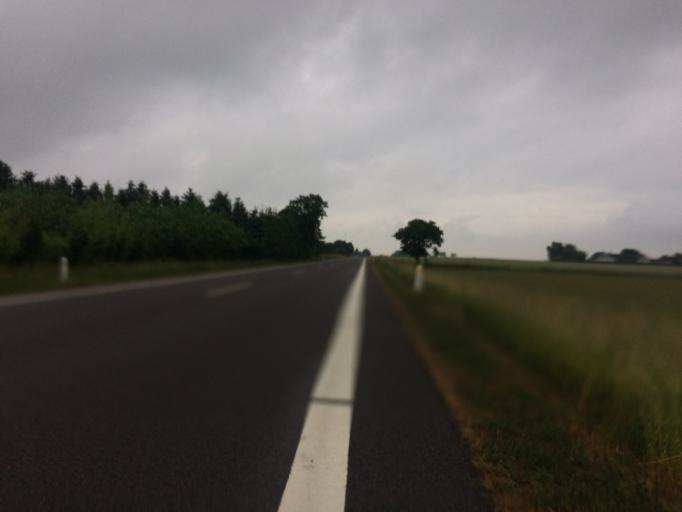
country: DK
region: Capital Region
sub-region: Bornholm Kommune
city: Akirkeby
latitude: 55.1351
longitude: 14.8413
